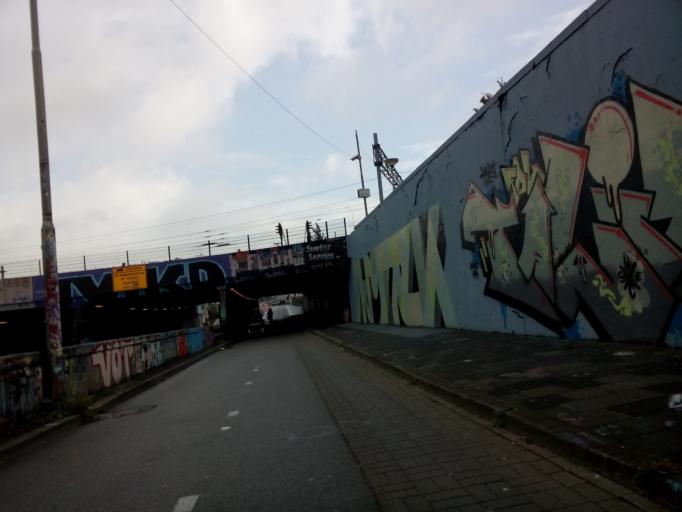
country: NL
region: South Holland
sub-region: Gemeente Delft
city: Delft
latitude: 52.0036
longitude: 4.3568
